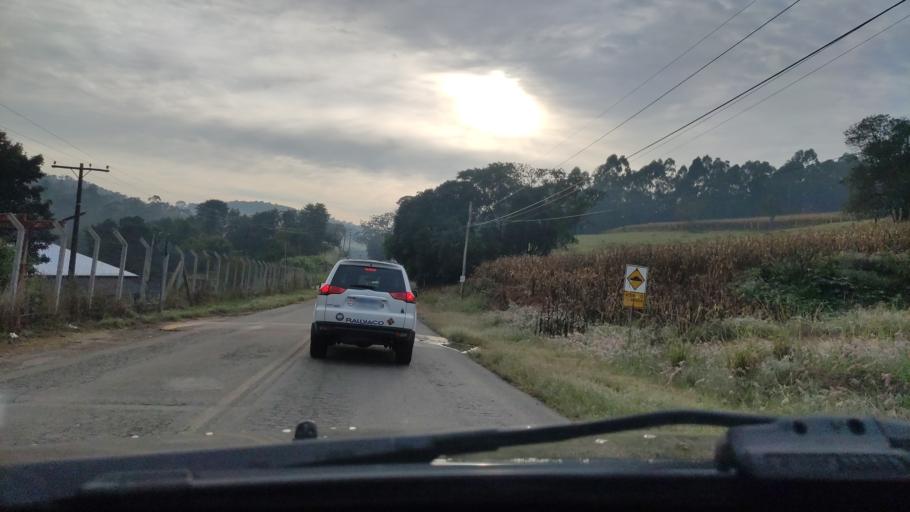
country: BR
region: Sao Paulo
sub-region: Jarinu
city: Jarinu
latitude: -23.1235
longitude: -46.7717
